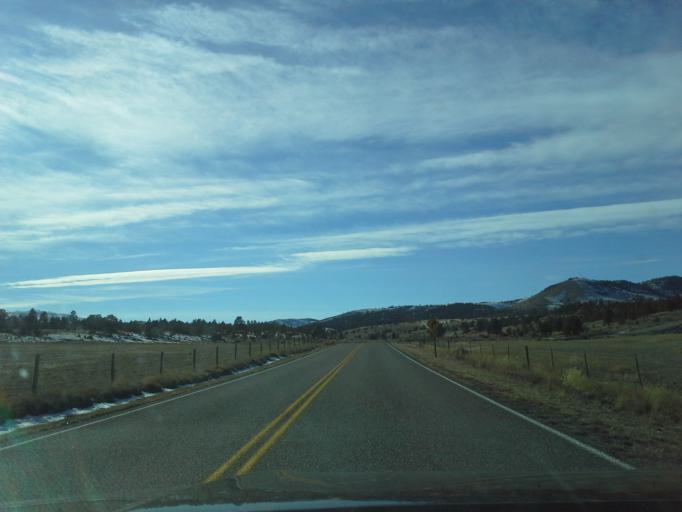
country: US
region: Montana
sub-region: Lewis and Clark County
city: Helena Valley Northeast
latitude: 46.8210
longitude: -111.9689
